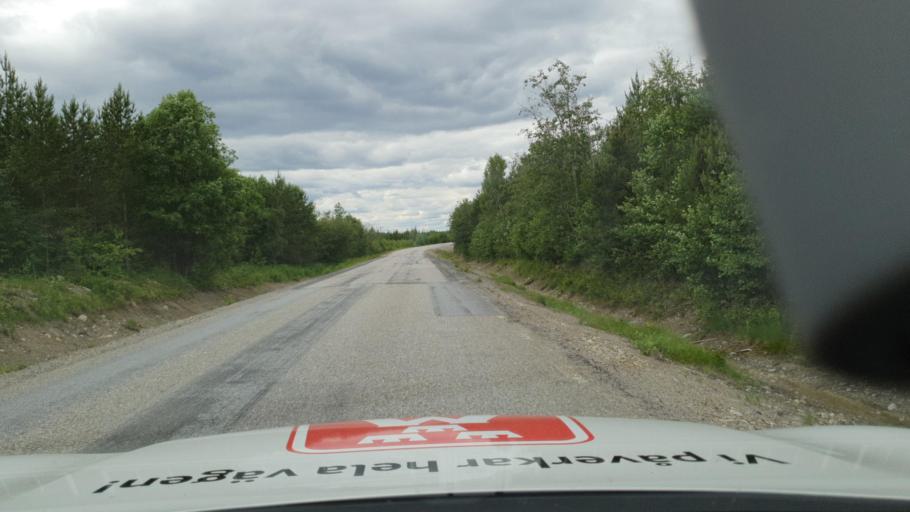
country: SE
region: Vaesterbotten
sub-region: Bjurholms Kommun
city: Bjurholm
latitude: 63.7692
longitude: 19.2522
